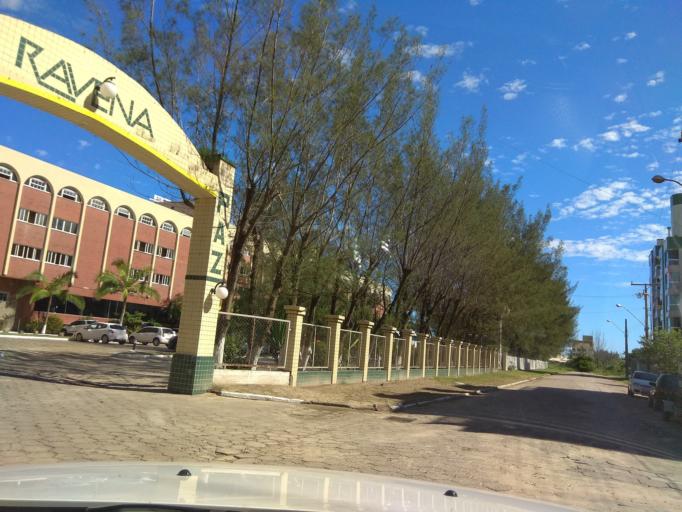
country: BR
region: Santa Catarina
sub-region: Laguna
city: Laguna
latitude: -28.4884
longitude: -48.7664
